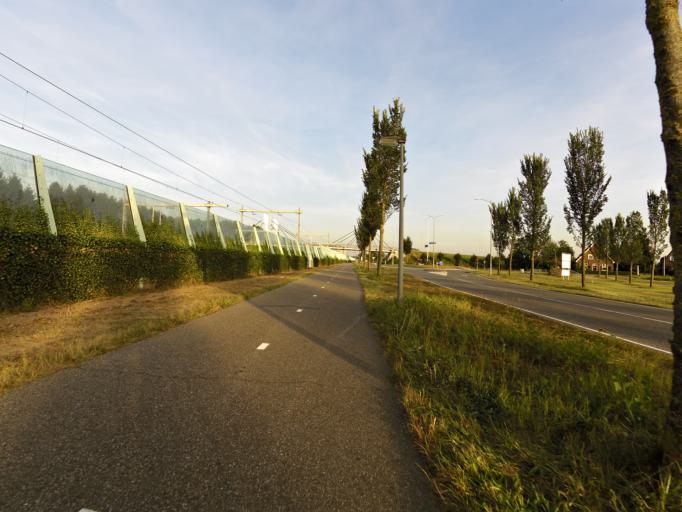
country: NL
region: Gelderland
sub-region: Gemeente Zevenaar
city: Zevenaar
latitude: 51.9189
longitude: 6.0877
